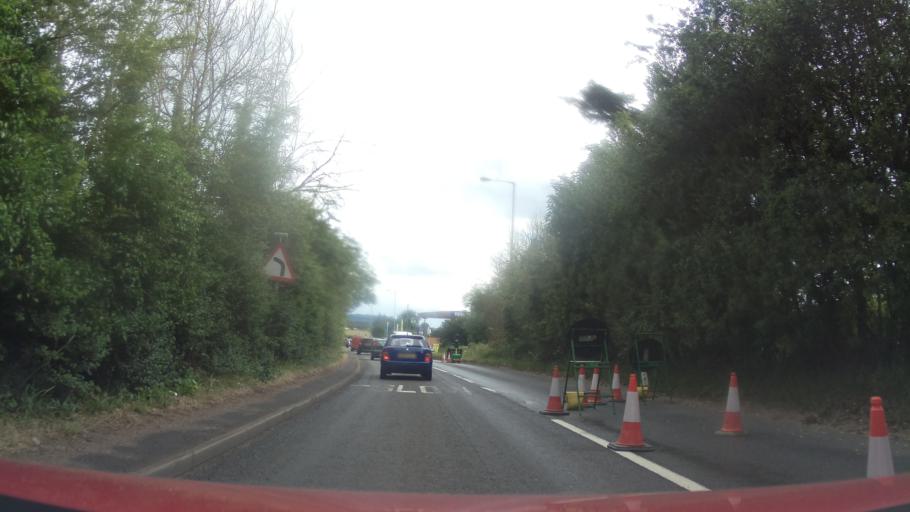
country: GB
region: England
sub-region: Dudley
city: Kingswinford
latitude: 52.5298
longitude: -2.1789
